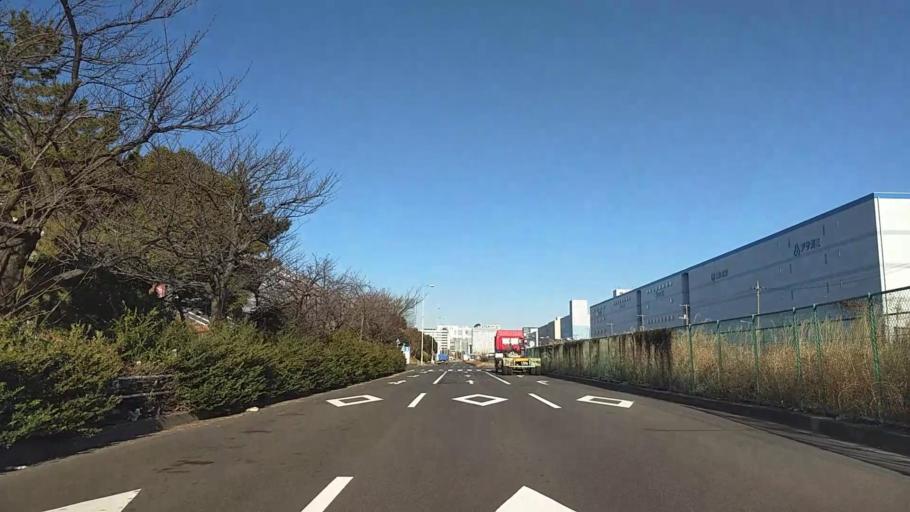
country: JP
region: Kanagawa
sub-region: Kawasaki-shi
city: Kawasaki
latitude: 35.6088
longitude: 139.7886
